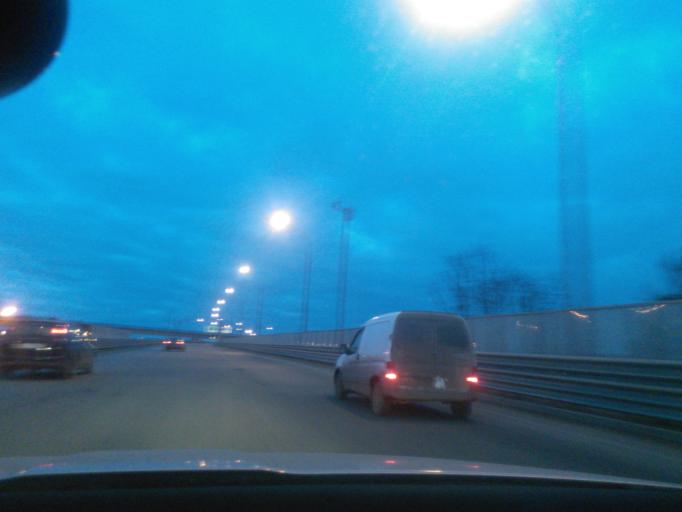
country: RU
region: Moskovskaya
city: Levoberezhnaya
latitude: 55.8844
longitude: 37.4735
